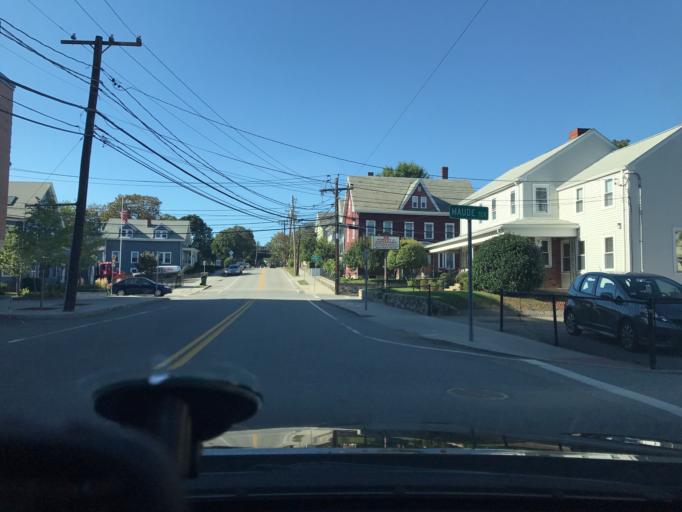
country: US
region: Massachusetts
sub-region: Middlesex County
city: Watertown
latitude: 42.3668
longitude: -71.1824
